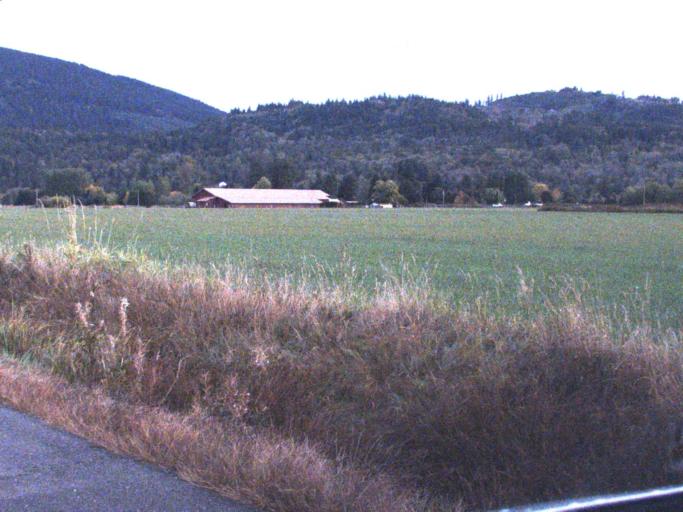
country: US
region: Washington
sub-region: Skagit County
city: Burlington
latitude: 48.5830
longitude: -122.4220
